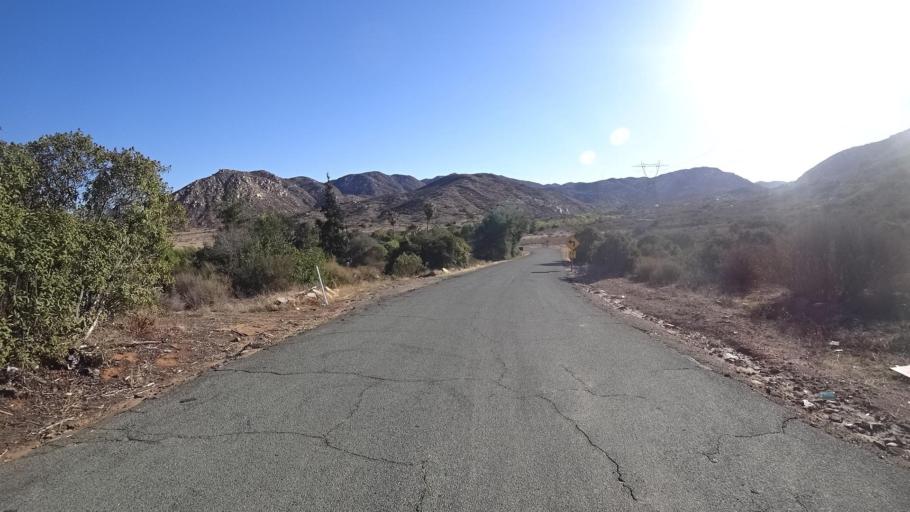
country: MX
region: Baja California
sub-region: Tecate
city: Lomas de Santa Anita
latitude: 32.6057
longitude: -116.6971
